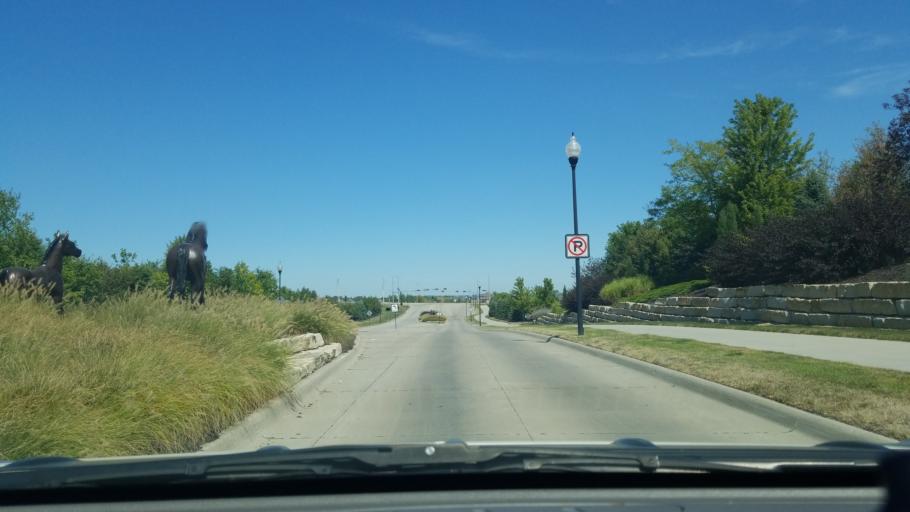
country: US
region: Nebraska
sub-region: Sarpy County
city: Papillion
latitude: 41.1449
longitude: -96.1008
